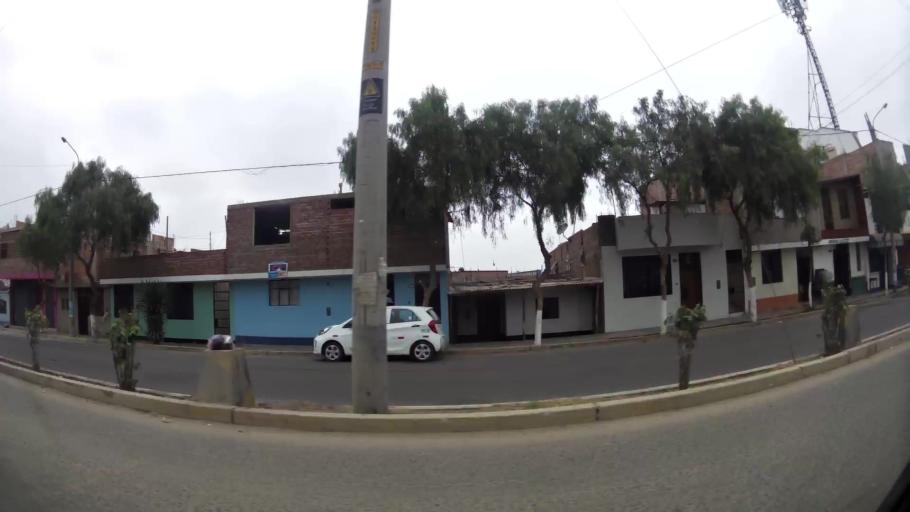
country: PE
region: La Libertad
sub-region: Provincia de Trujillo
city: La Esperanza
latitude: -8.0917
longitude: -79.0398
